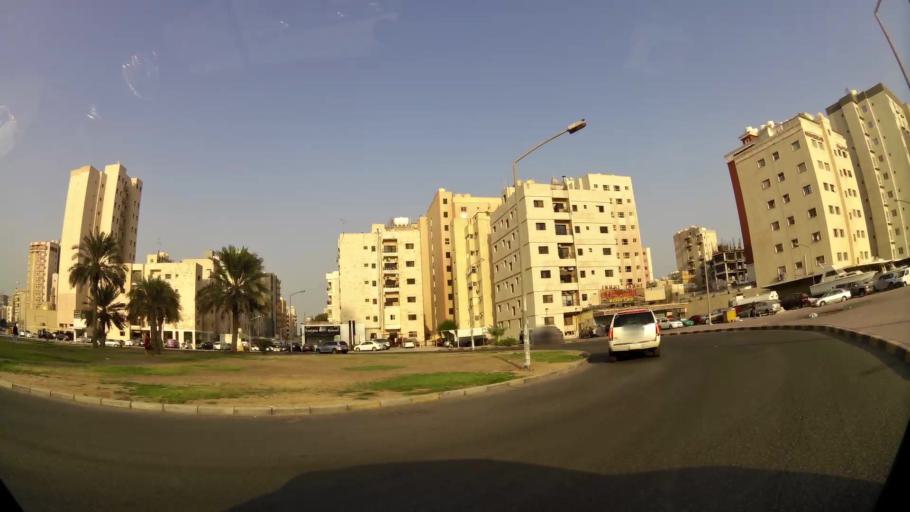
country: KW
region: Muhafazat Hawalli
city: As Salimiyah
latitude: 29.3272
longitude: 48.0672
